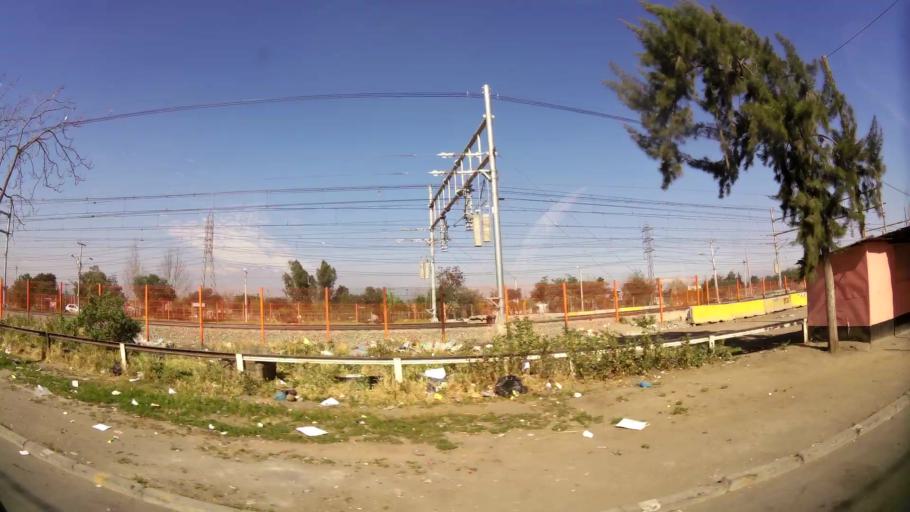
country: CL
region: Santiago Metropolitan
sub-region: Provincia de Santiago
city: Santiago
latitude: -33.5127
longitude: -70.6858
